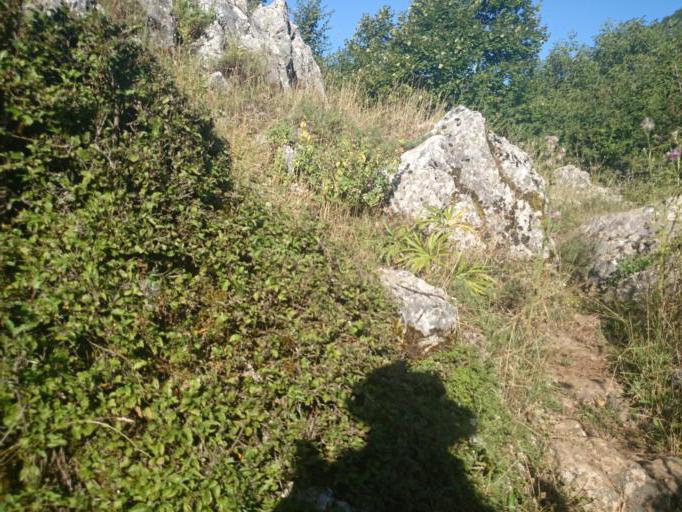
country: AL
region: Diber
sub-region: Rrethi i Bulqizes
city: Martanesh
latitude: 41.4013
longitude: 20.1700
